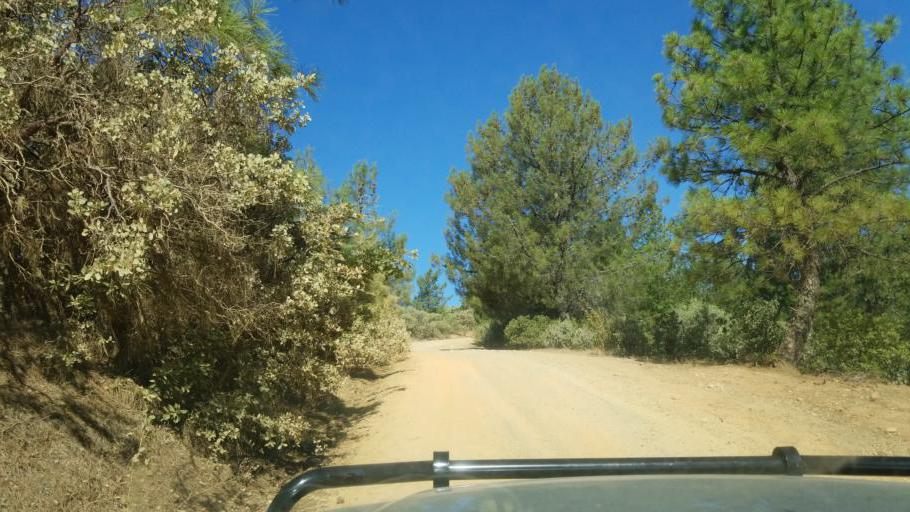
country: US
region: California
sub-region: Shasta County
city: Shasta
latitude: 40.6592
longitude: -122.4649
